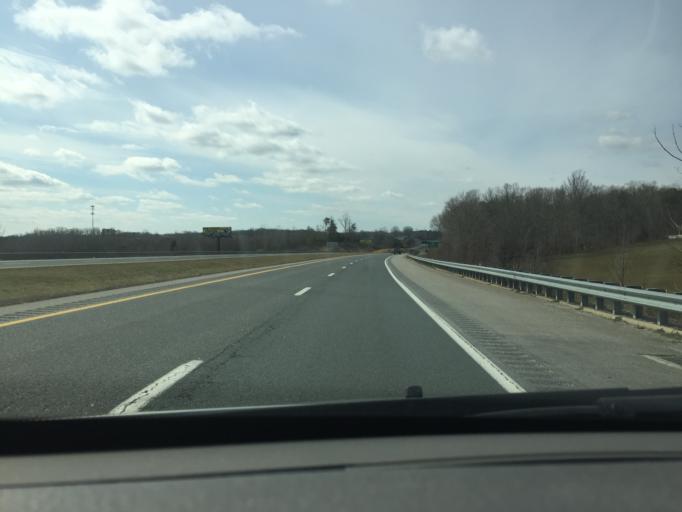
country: US
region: Virginia
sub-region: Campbell County
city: Timberlake
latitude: 37.3218
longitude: -79.2180
